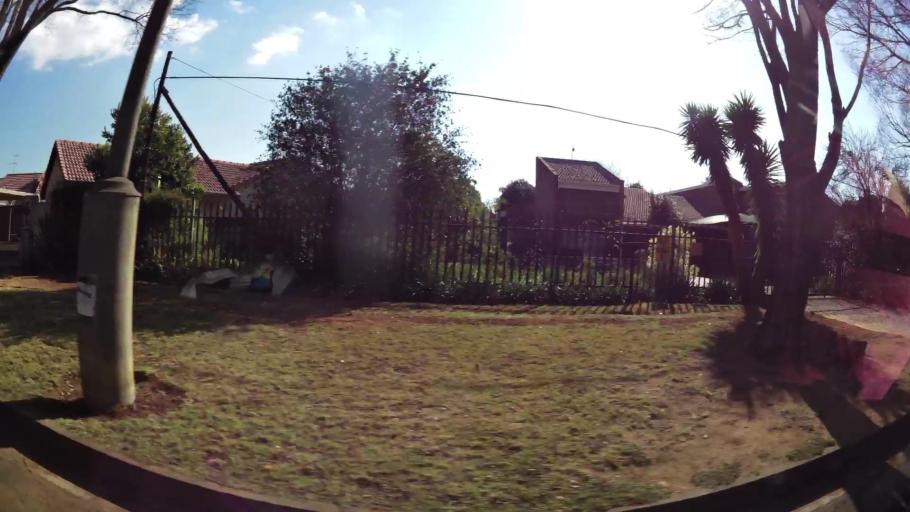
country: ZA
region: Gauteng
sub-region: Ekurhuleni Metropolitan Municipality
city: Benoni
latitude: -26.1451
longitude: 28.3371
